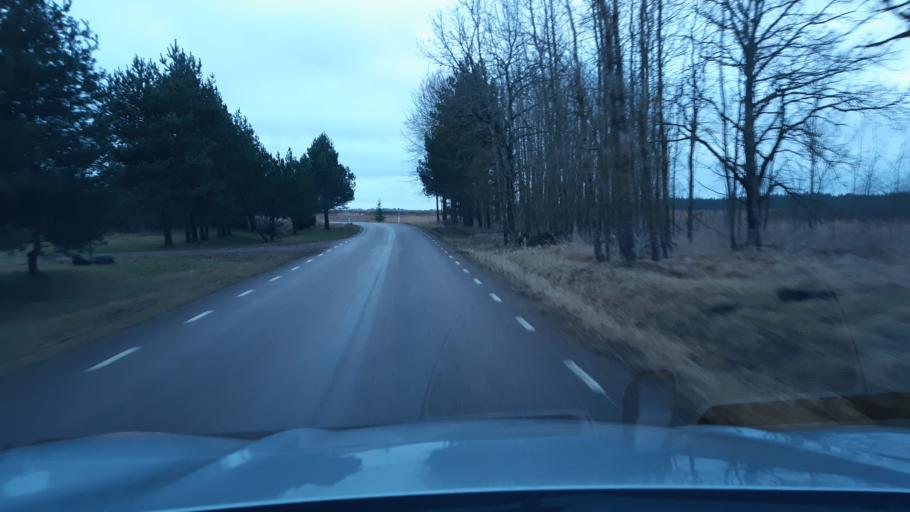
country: EE
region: Raplamaa
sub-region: Rapla vald
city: Rapla
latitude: 59.0002
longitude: 24.7166
